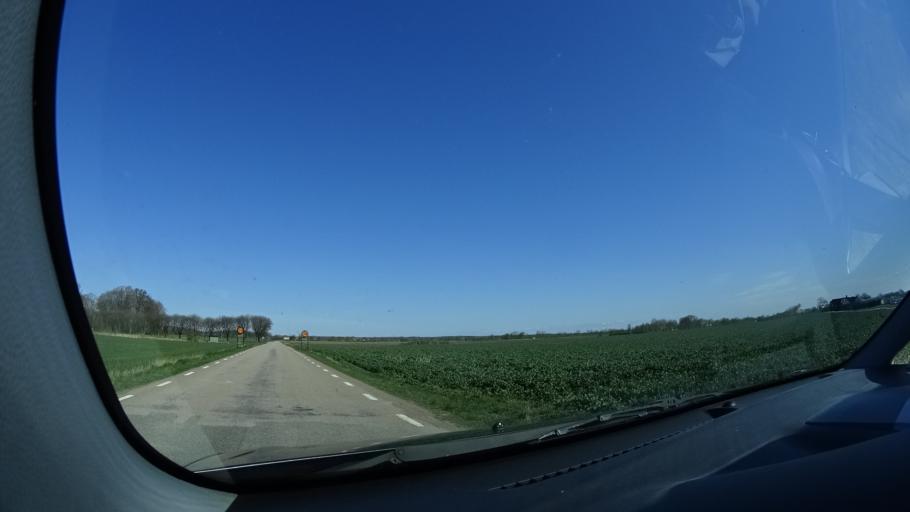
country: SE
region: Skane
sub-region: Hoganas Kommun
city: Hoganas
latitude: 56.2125
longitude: 12.5945
